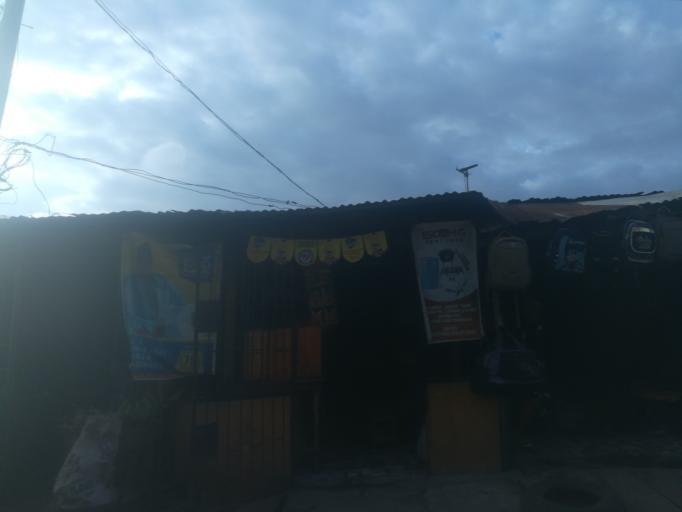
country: NG
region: Lagos
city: Somolu
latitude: 6.5428
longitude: 3.3872
